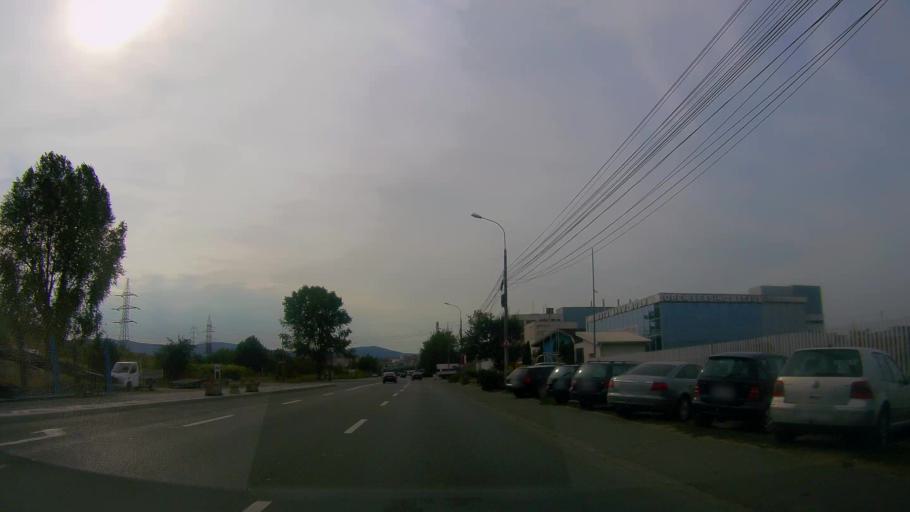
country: RO
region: Salaj
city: Zalau
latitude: 47.2120
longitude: 23.0435
